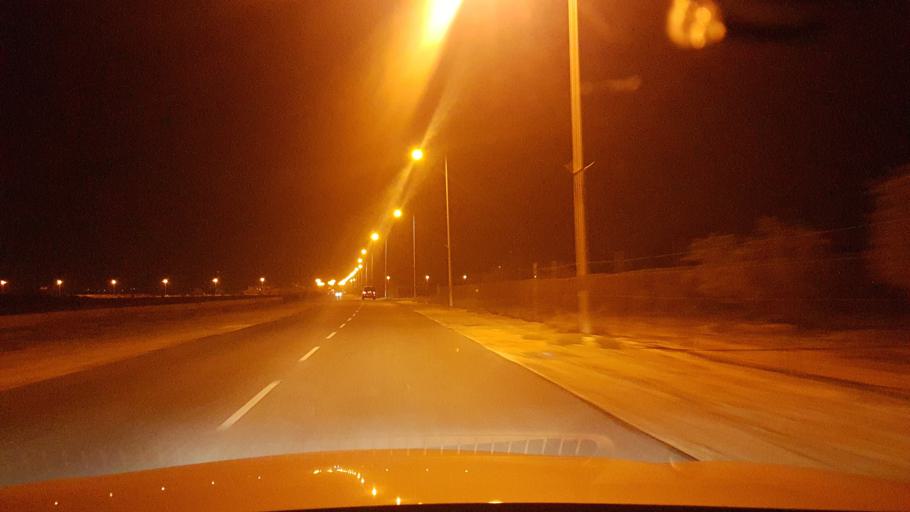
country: BH
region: Central Governorate
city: Dar Kulayb
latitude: 26.0222
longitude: 50.4813
